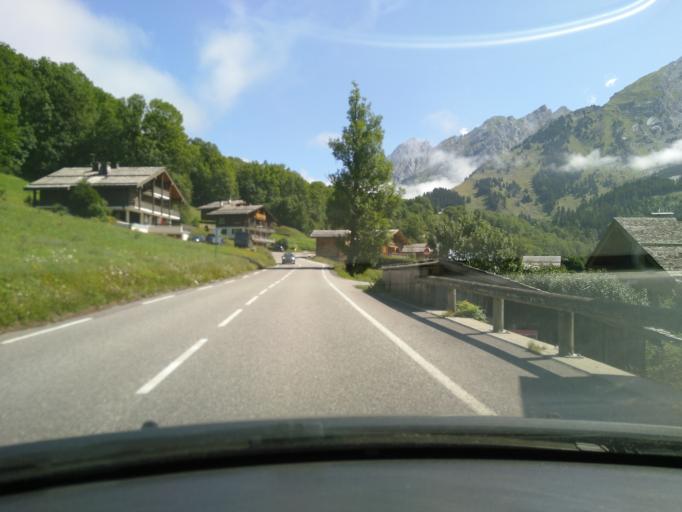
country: FR
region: Rhone-Alpes
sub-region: Departement de la Haute-Savoie
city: La Clusaz
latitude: 45.9097
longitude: 6.4525
